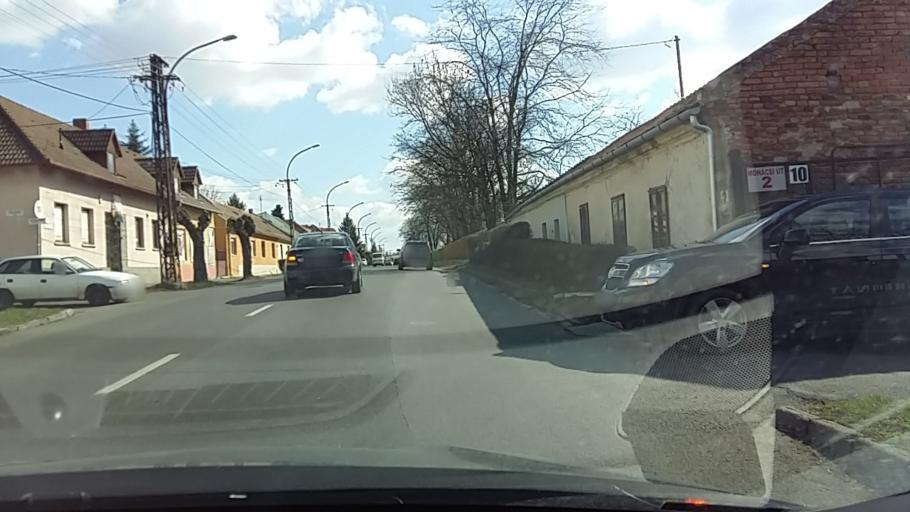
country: HU
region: Baranya
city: Pecs
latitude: 46.0794
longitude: 18.2611
